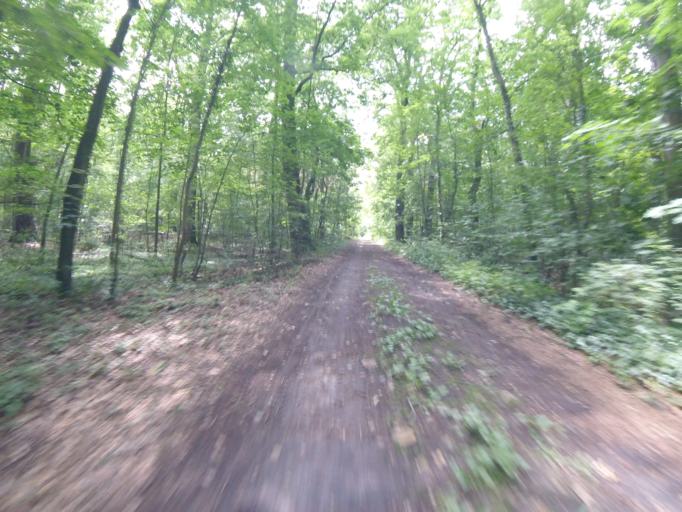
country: DE
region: Brandenburg
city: Konigs Wusterhausen
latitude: 52.2908
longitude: 13.6433
